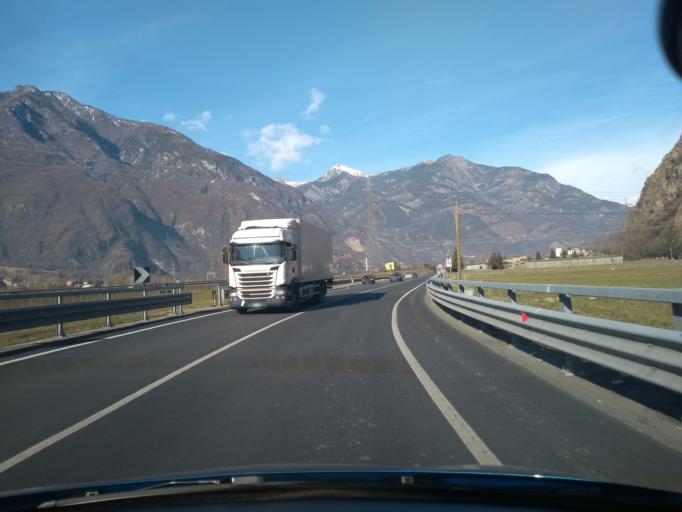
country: IT
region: Aosta Valley
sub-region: Valle d'Aosta
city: Issogne
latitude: 45.6551
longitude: 7.6994
